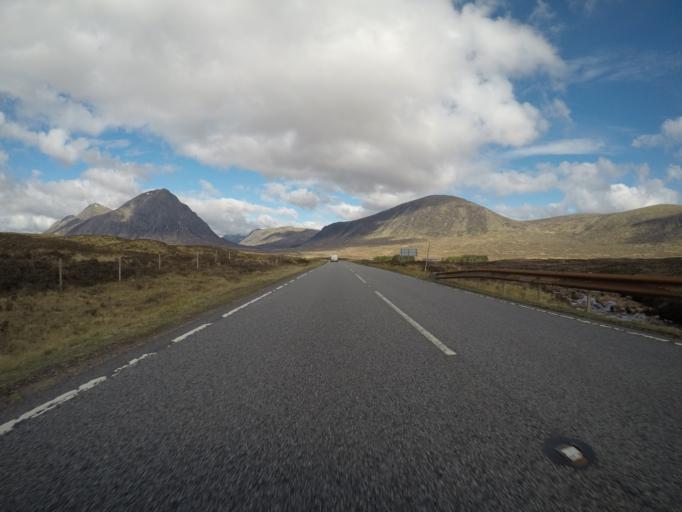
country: GB
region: Scotland
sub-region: Highland
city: Spean Bridge
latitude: 56.6454
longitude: -4.8330
